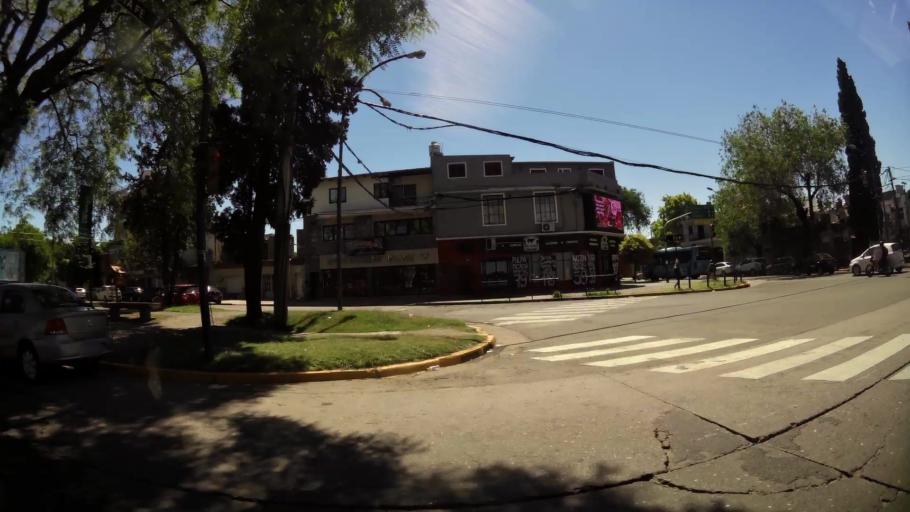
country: AR
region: Santa Fe
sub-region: Departamento de Rosario
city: Rosario
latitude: -32.9380
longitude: -60.6789
